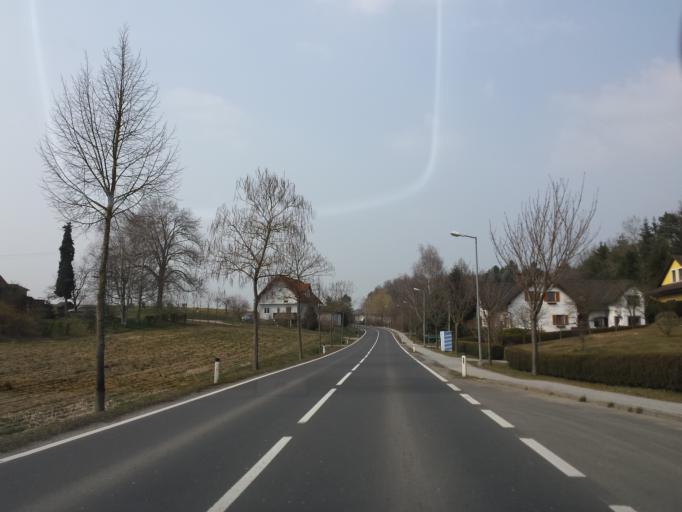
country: AT
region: Styria
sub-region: Politischer Bezirk Hartberg-Fuerstenfeld
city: Fuerstenfeld
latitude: 47.0265
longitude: 16.0924
